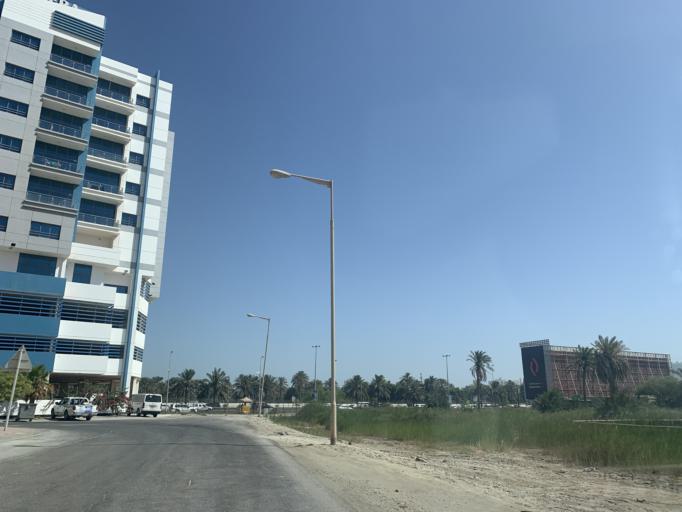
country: BH
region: Manama
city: Jidd Hafs
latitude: 26.2259
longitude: 50.5275
